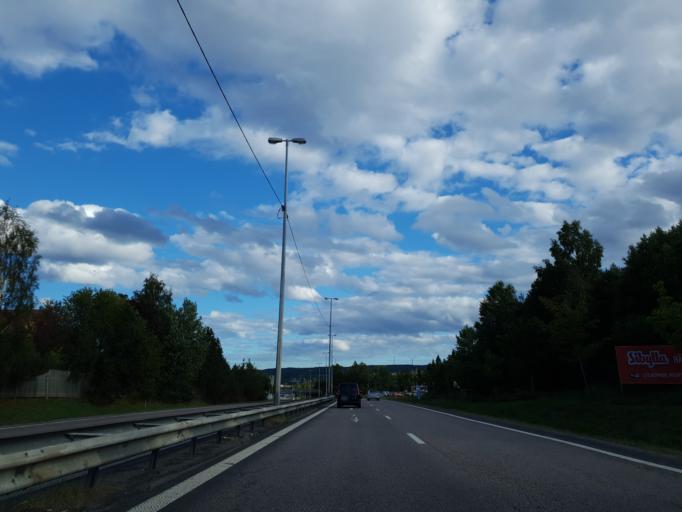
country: SE
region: Vaesternorrland
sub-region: Haernoesands Kommun
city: Haernoesand
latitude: 62.6421
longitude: 17.9121
